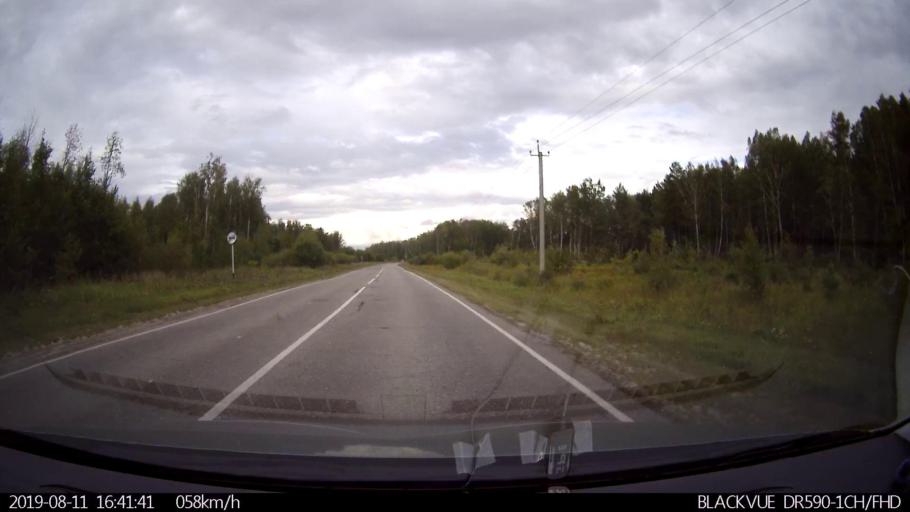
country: RU
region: Ulyanovsk
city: Mayna
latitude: 54.1550
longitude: 47.6550
